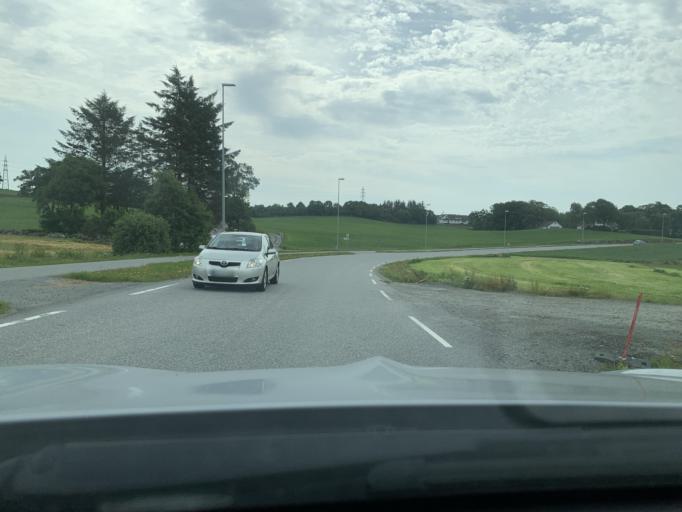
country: NO
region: Rogaland
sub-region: Time
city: Bryne
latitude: 58.7422
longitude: 5.6900
